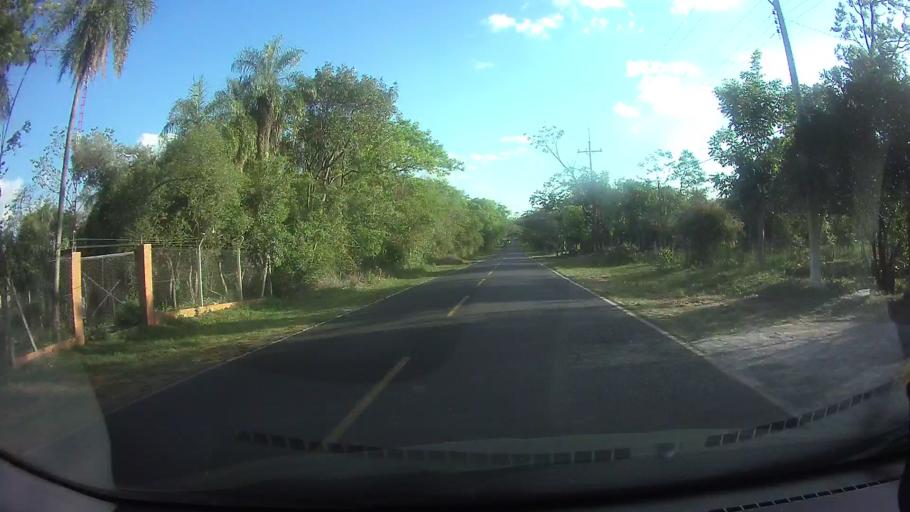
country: PY
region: Cordillera
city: Emboscada
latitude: -25.1900
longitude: -57.3182
